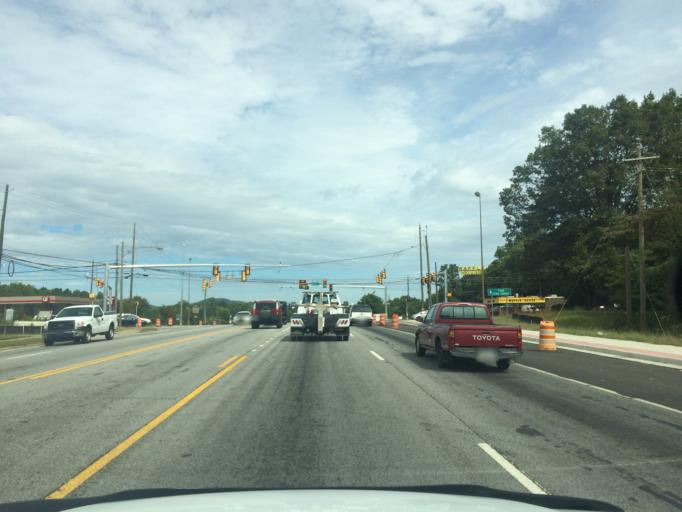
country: US
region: Georgia
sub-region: Cobb County
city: Fair Oaks
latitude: 33.9179
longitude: -84.5489
